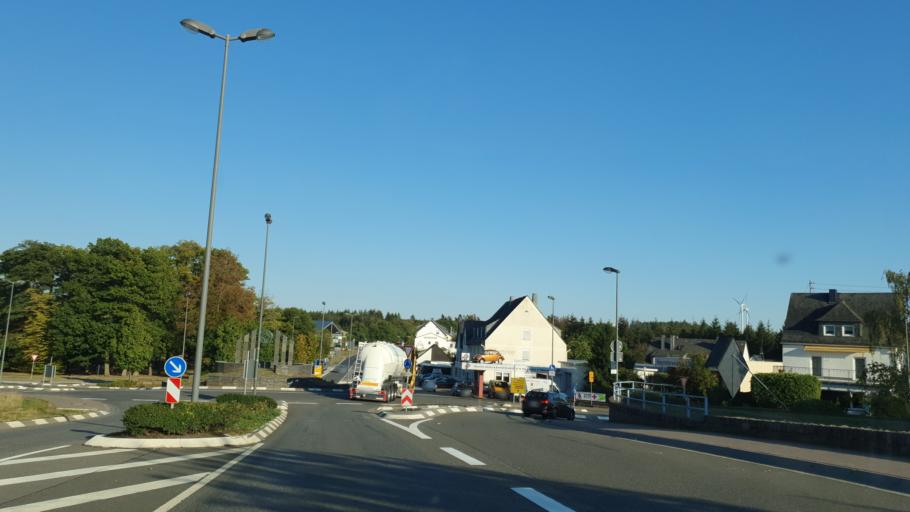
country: DE
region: Rheinland-Pfalz
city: Kratzenburg
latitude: 50.2146
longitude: 7.5455
